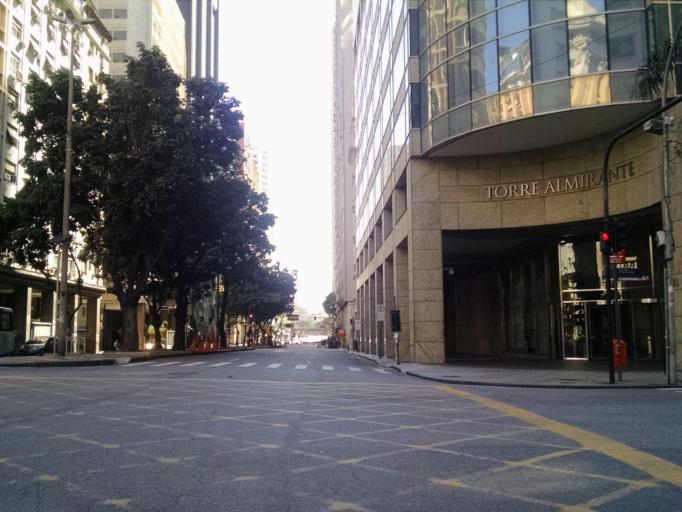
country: BR
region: Rio de Janeiro
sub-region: Rio De Janeiro
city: Rio de Janeiro
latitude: -22.9075
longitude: -43.1749
